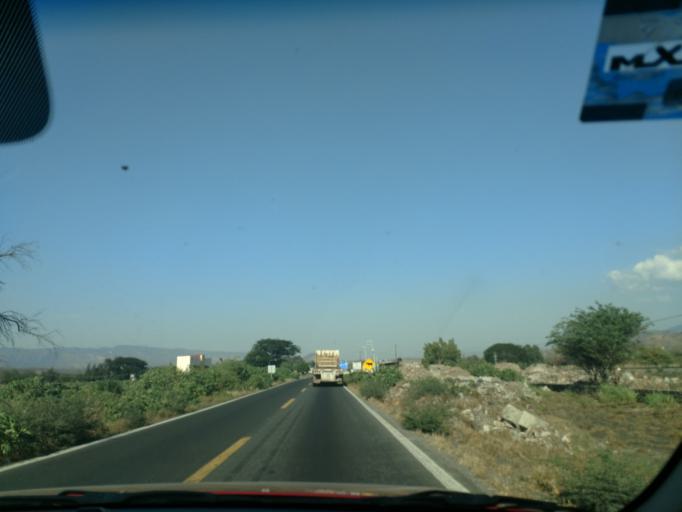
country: MX
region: Nayarit
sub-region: Ahuacatlan
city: Ahuacatlan
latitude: 21.0595
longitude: -104.5011
